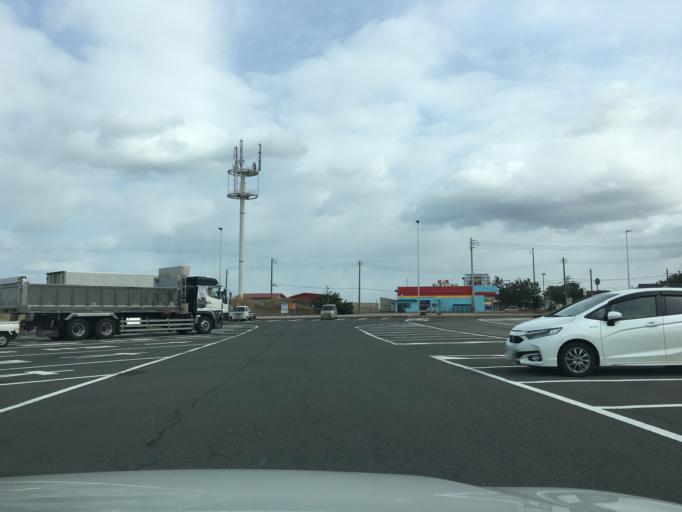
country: JP
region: Yamagata
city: Yuza
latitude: 39.2205
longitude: 139.9010
